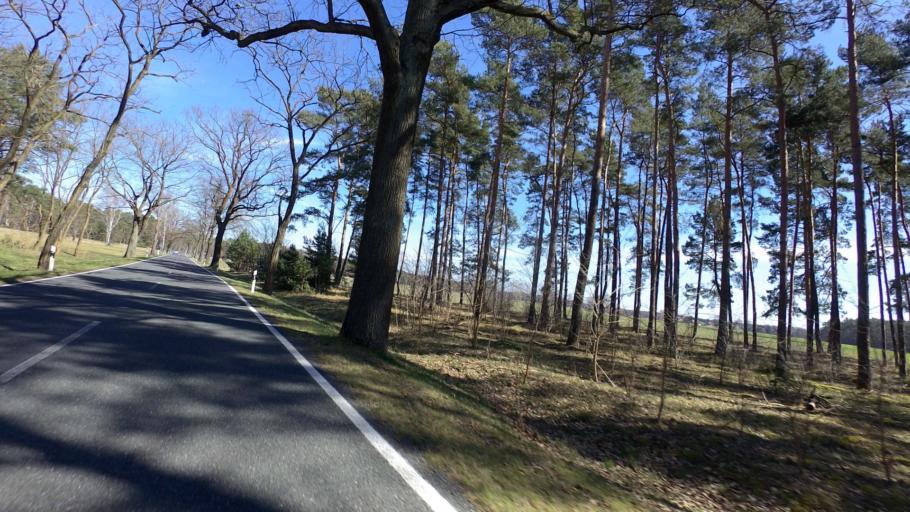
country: DE
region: Brandenburg
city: Munchehofe
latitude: 52.1225
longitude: 13.7979
